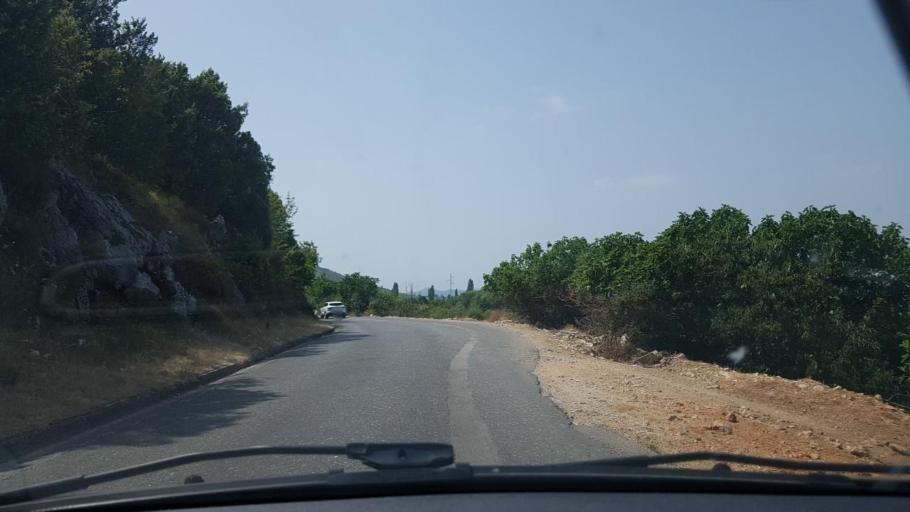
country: BA
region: Federation of Bosnia and Herzegovina
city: Tasovcici
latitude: 43.0331
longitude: 17.7368
